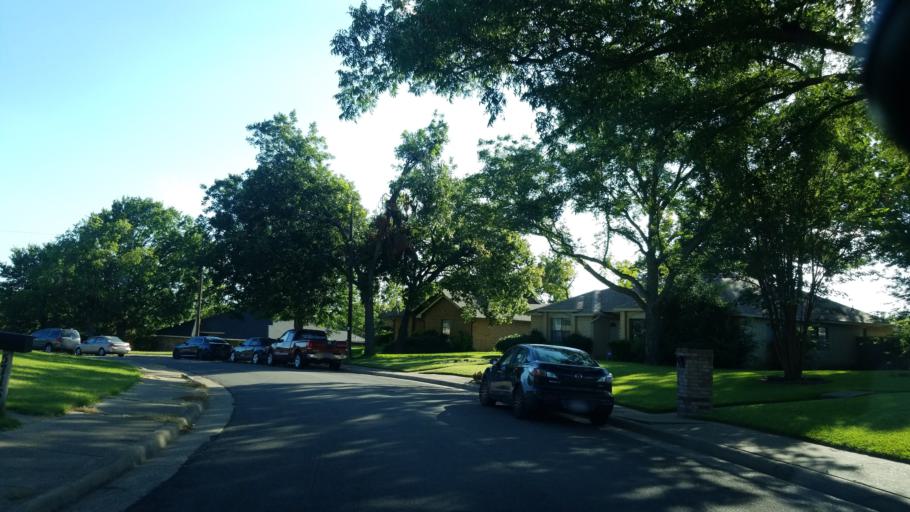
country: US
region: Texas
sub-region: Dallas County
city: Balch Springs
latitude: 32.7820
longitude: -96.7045
